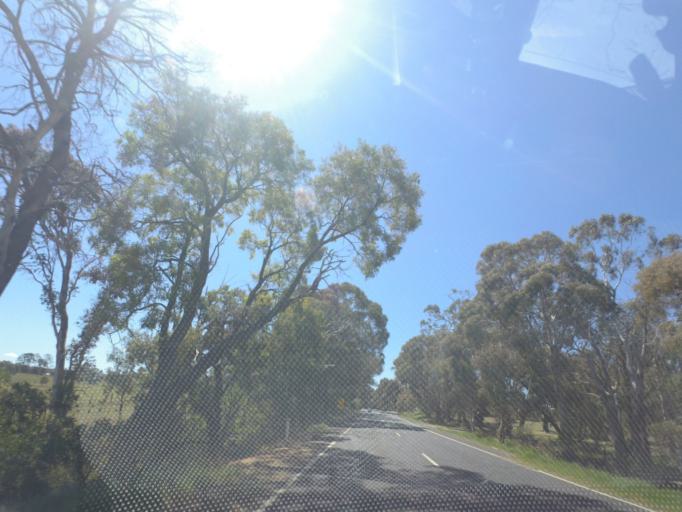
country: AU
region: Victoria
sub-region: Hume
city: Sunbury
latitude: -37.2495
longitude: 144.7389
